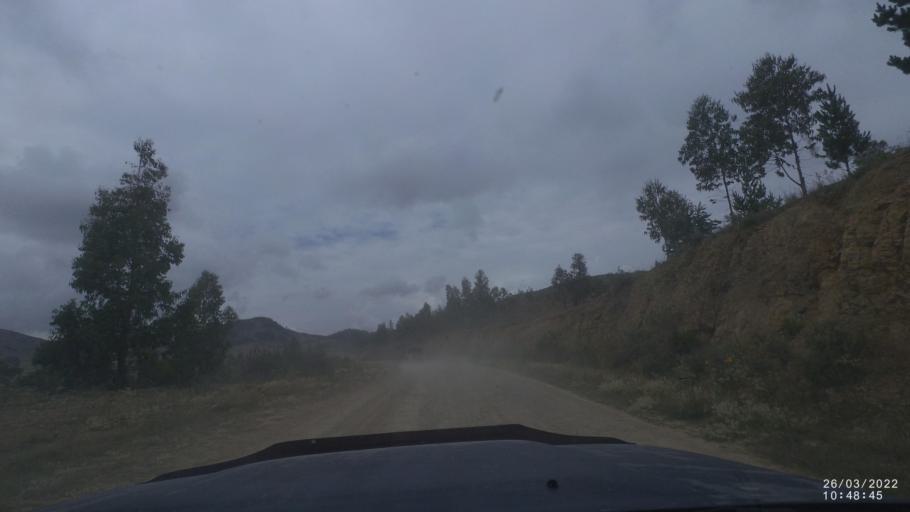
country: BO
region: Cochabamba
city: Tarata
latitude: -17.4978
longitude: -66.0425
